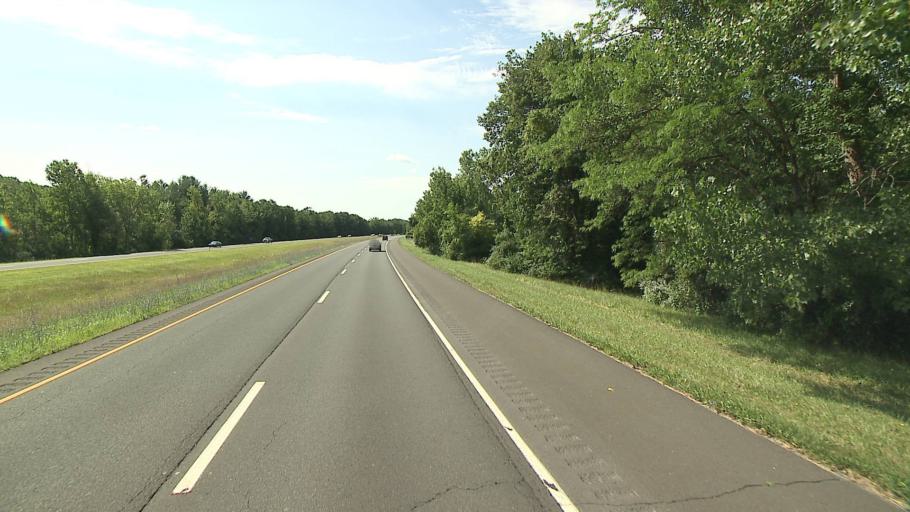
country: US
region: Connecticut
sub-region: Fairfield County
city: Danbury
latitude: 41.4555
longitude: -73.3962
